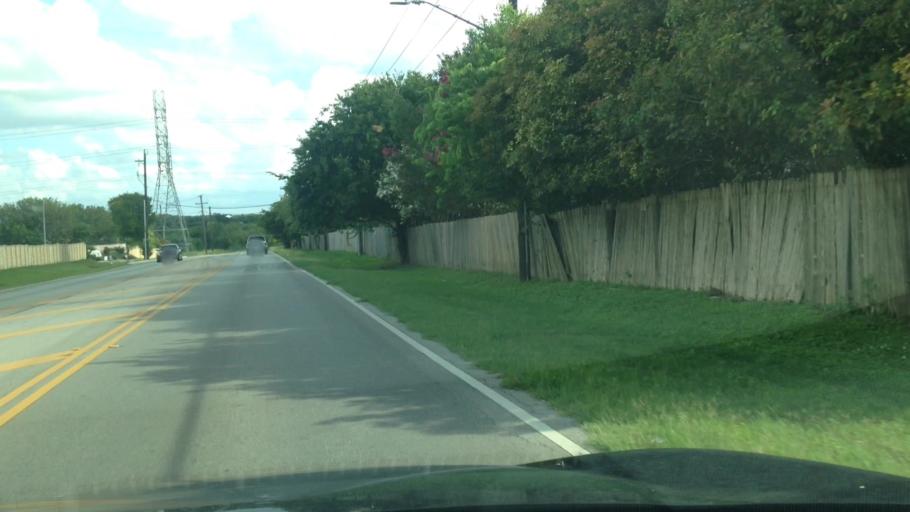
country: US
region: Texas
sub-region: Bexar County
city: Live Oak
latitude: 29.5845
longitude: -98.4051
